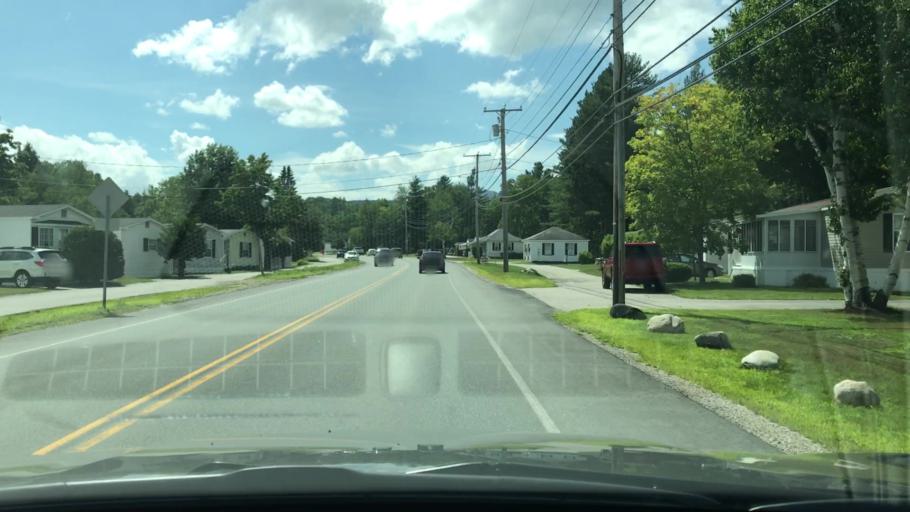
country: US
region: New Hampshire
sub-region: Coos County
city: Gorham
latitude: 44.3998
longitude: -71.2143
